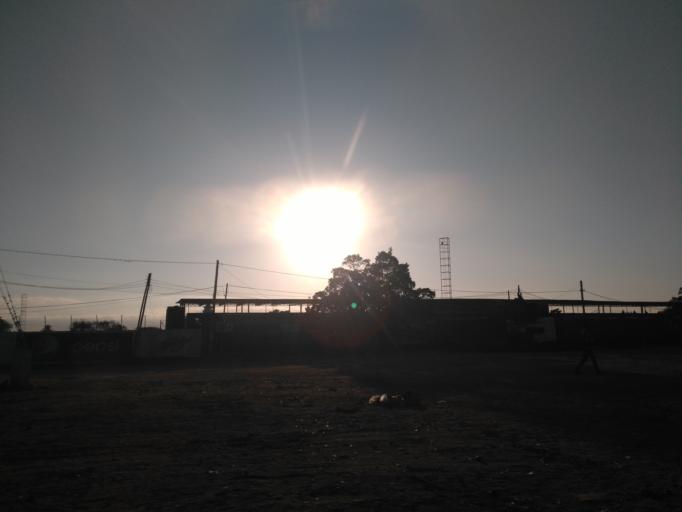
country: TZ
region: Dodoma
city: Dodoma
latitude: -6.1732
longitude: 35.7426
